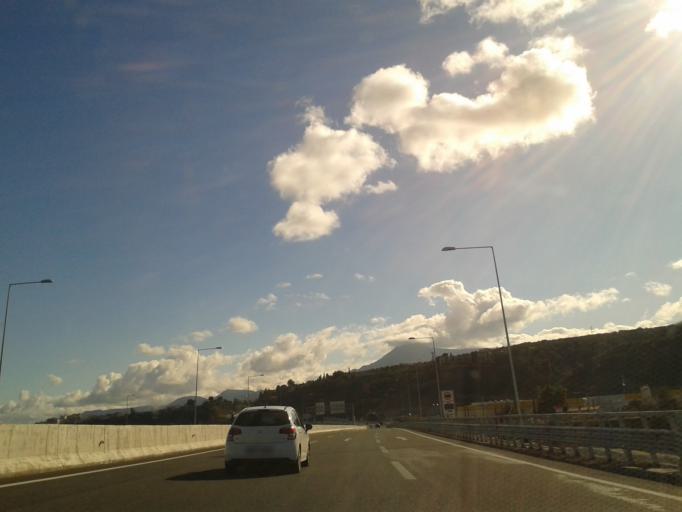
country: GR
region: West Greece
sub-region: Nomos Achaias
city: Aigio
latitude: 38.2624
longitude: 22.0593
